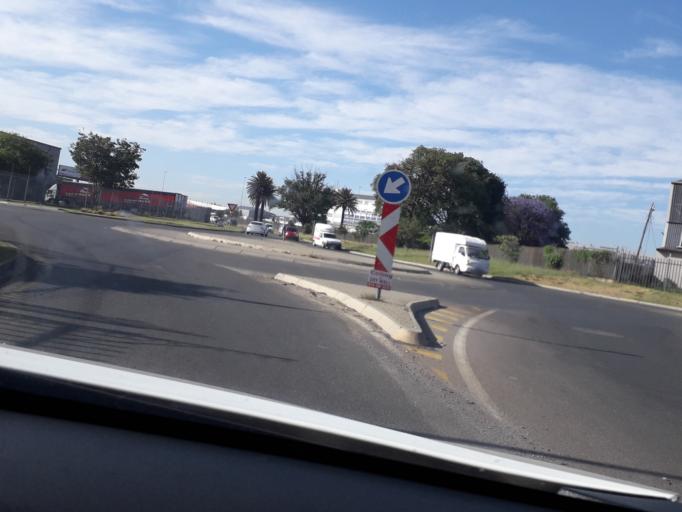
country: ZA
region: Gauteng
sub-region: Ekurhuleni Metropolitan Municipality
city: Germiston
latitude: -26.1638
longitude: 28.1887
